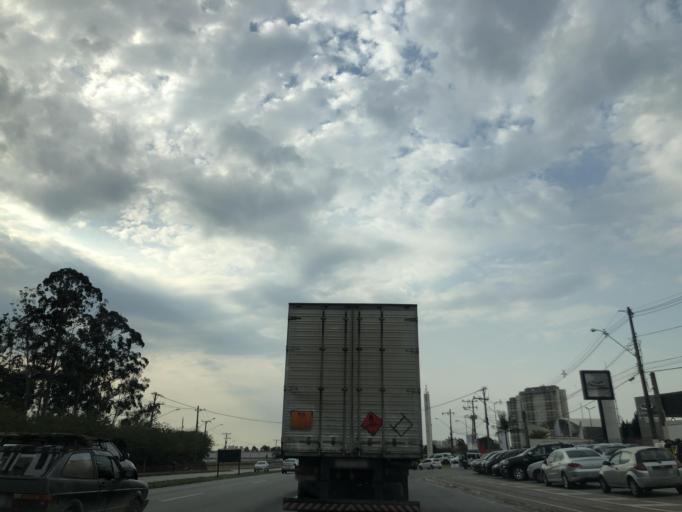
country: BR
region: Sao Paulo
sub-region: Sorocaba
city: Sorocaba
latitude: -23.5363
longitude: -47.4881
